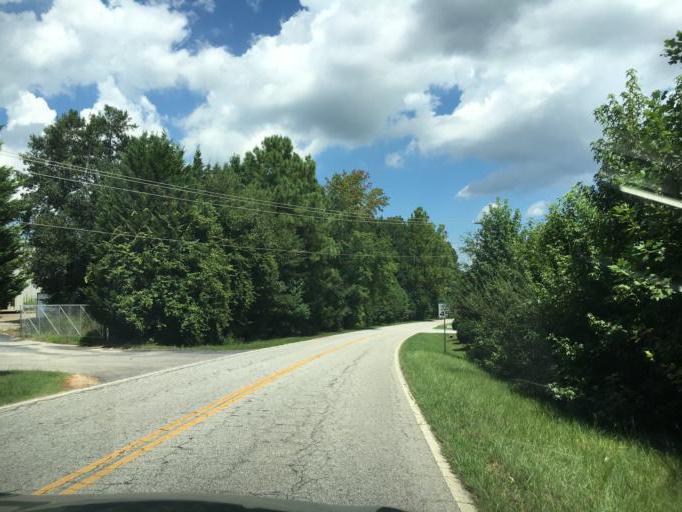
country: US
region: South Carolina
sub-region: Spartanburg County
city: Duncan
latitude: 34.8941
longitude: -82.1411
